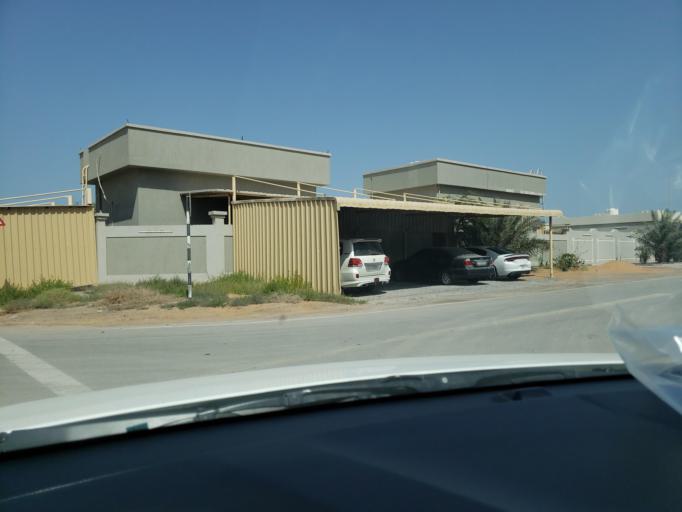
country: AE
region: Ra's al Khaymah
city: Ras al-Khaimah
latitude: 25.8554
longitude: 56.0178
